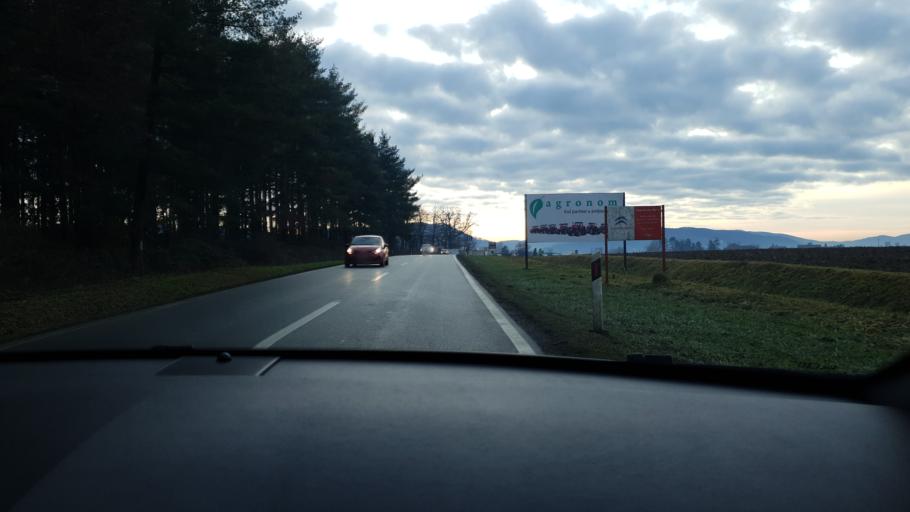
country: HR
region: Pozesko-Slavonska
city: Vidovci
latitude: 45.3468
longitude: 17.7185
